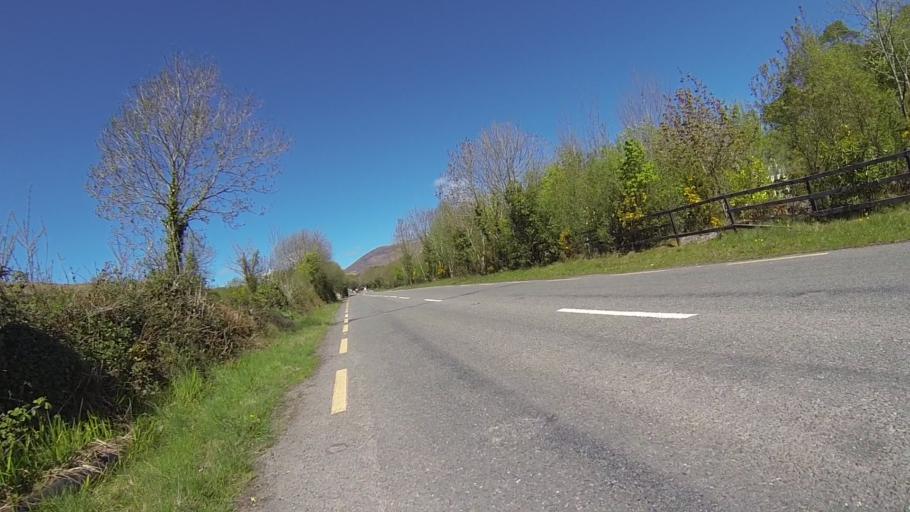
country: IE
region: Munster
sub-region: Ciarrai
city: Kenmare
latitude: 51.8904
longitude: -9.5988
